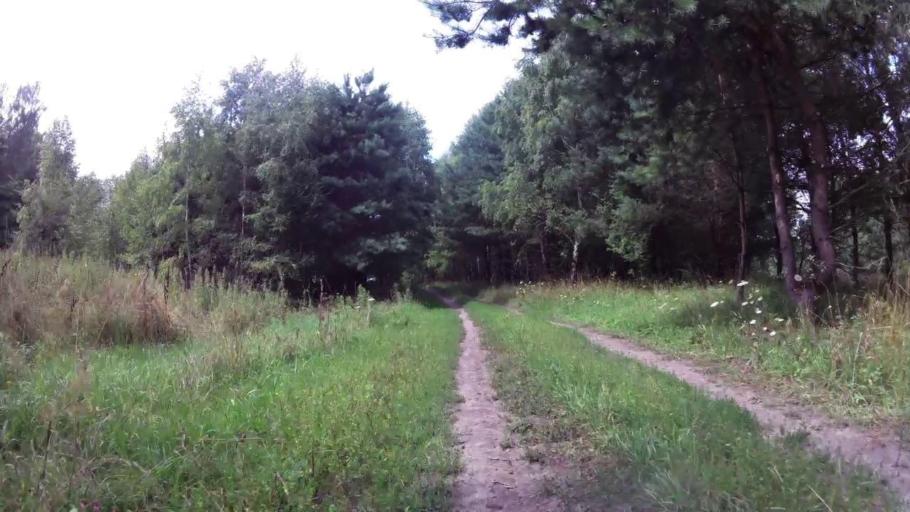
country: PL
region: West Pomeranian Voivodeship
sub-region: Powiat lobeski
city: Wegorzyno
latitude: 53.5277
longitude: 15.6183
